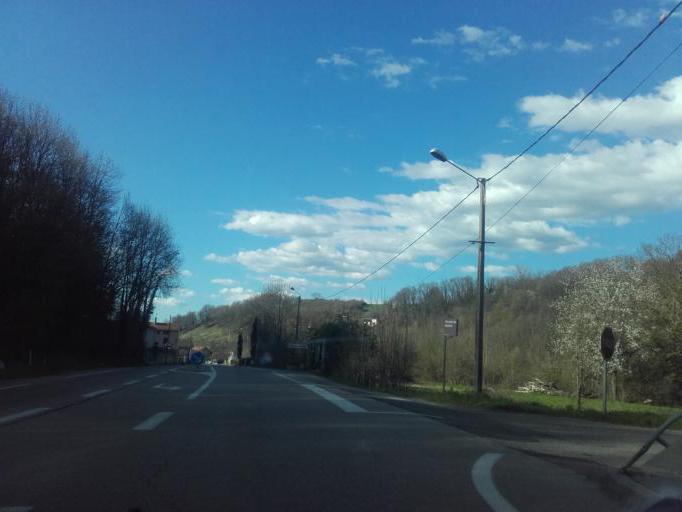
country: FR
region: Rhone-Alpes
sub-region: Departement de l'Isere
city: Nivolas-Vermelle
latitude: 45.5465
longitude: 5.3102
